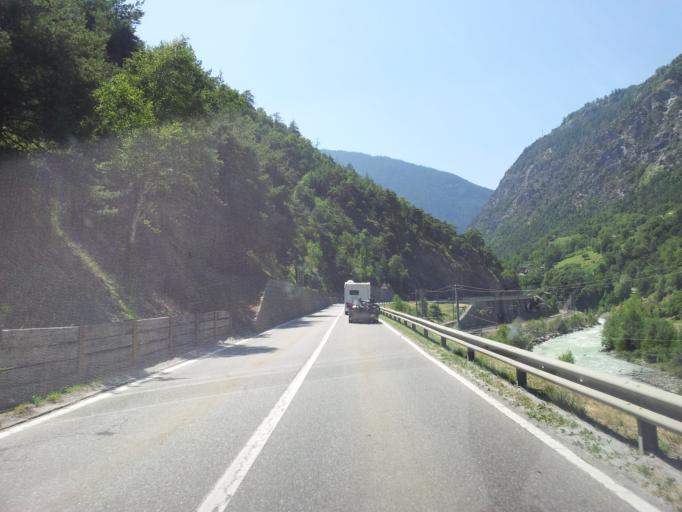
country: CH
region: Valais
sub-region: Visp District
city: Visperterminen
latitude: 46.2567
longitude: 7.8799
